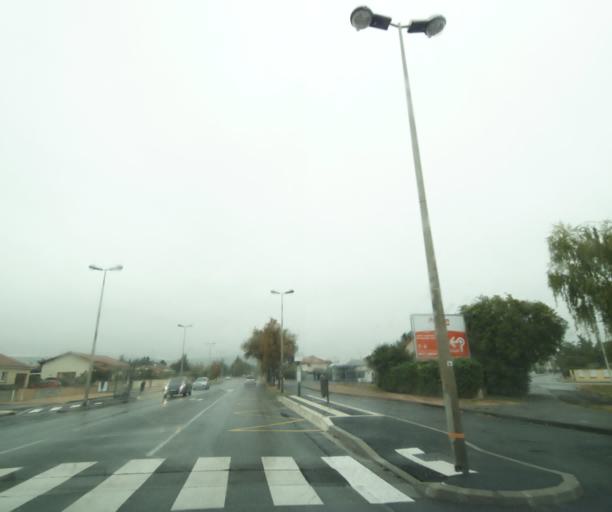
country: FR
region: Auvergne
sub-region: Departement du Puy-de-Dome
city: Cebazat
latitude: 45.8324
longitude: 3.1053
